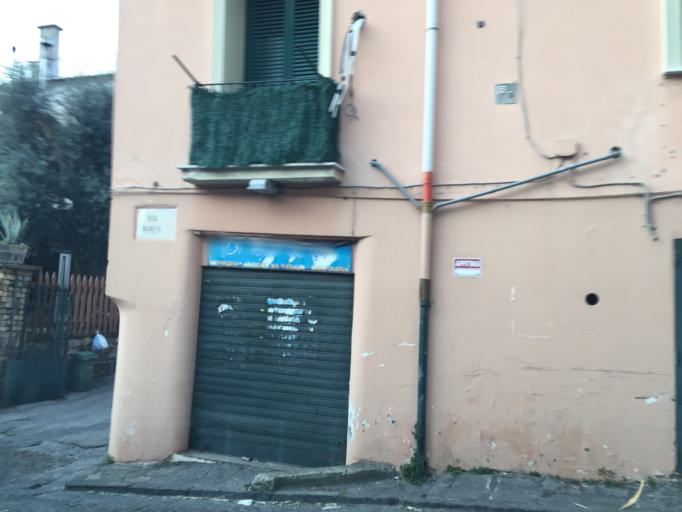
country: IT
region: Campania
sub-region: Provincia di Napoli
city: Castellammare di Stabia
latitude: 40.6891
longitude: 14.4819
